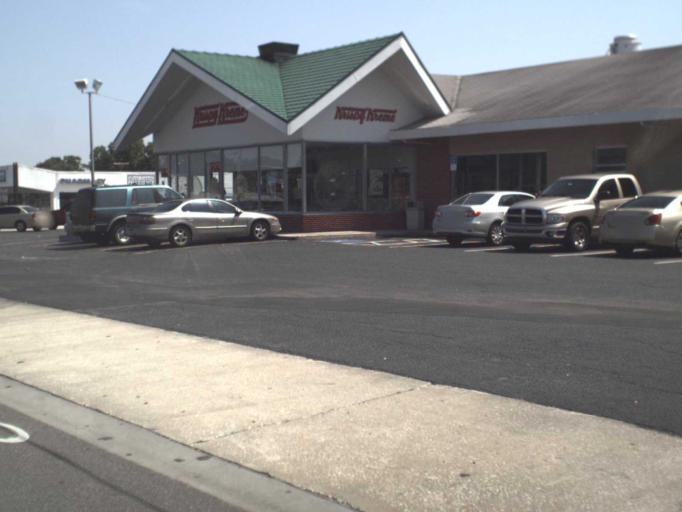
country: US
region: Florida
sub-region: Hillsborough County
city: Carrollwood
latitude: 28.0262
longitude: -82.4594
